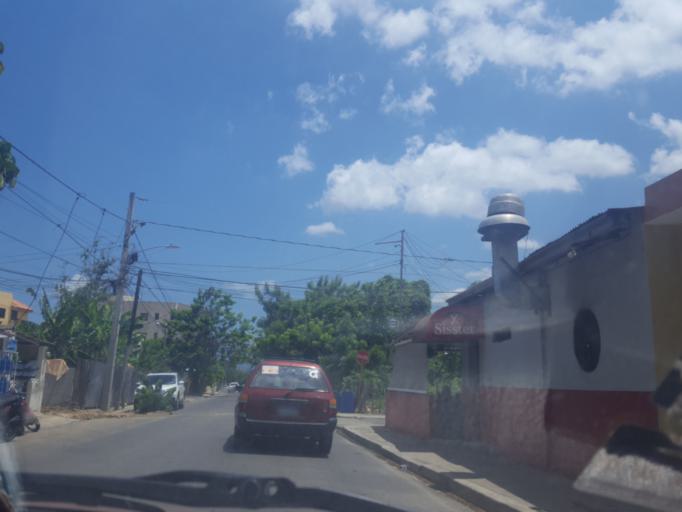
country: DO
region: Santiago
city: Santiago de los Caballeros
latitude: 19.4773
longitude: -70.6603
